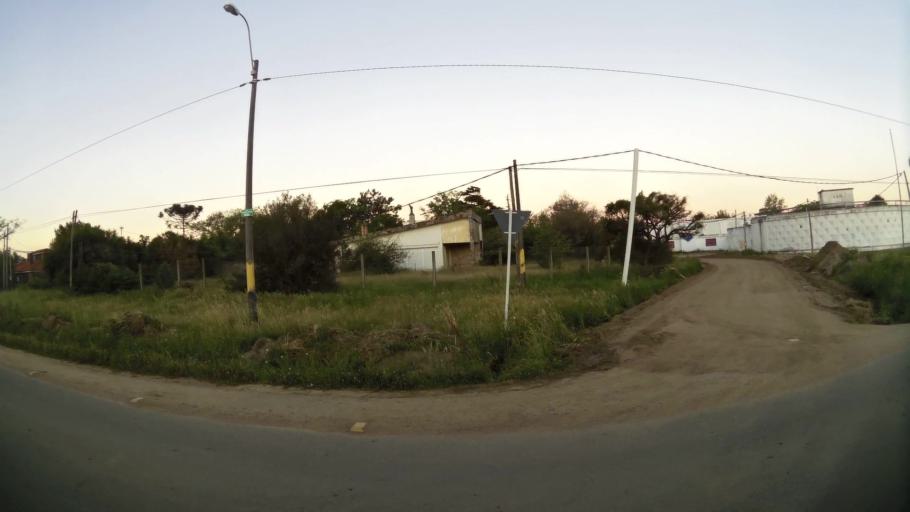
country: UY
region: Canelones
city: Barra de Carrasco
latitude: -34.8295
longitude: -55.9558
